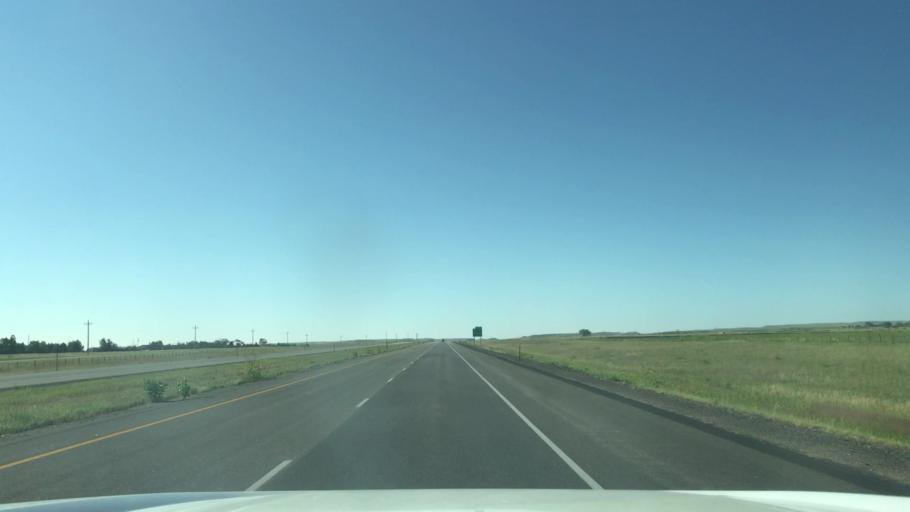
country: US
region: Wyoming
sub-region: Platte County
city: Wheatland
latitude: 41.9849
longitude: -104.9558
